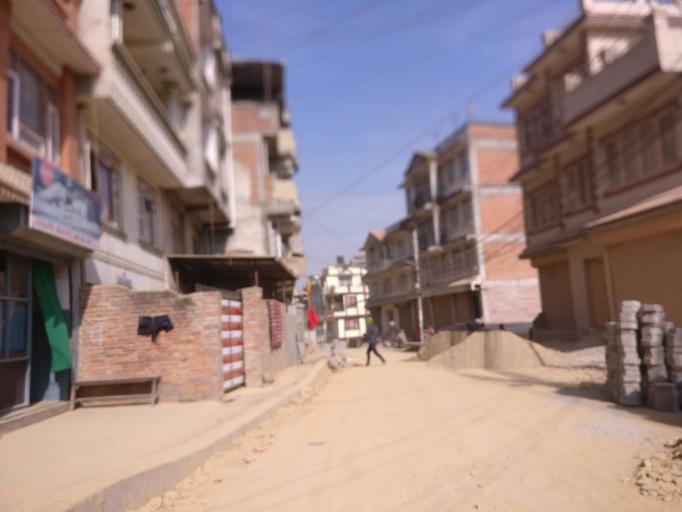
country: NP
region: Central Region
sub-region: Bagmati Zone
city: Patan
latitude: 27.6709
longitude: 85.3342
